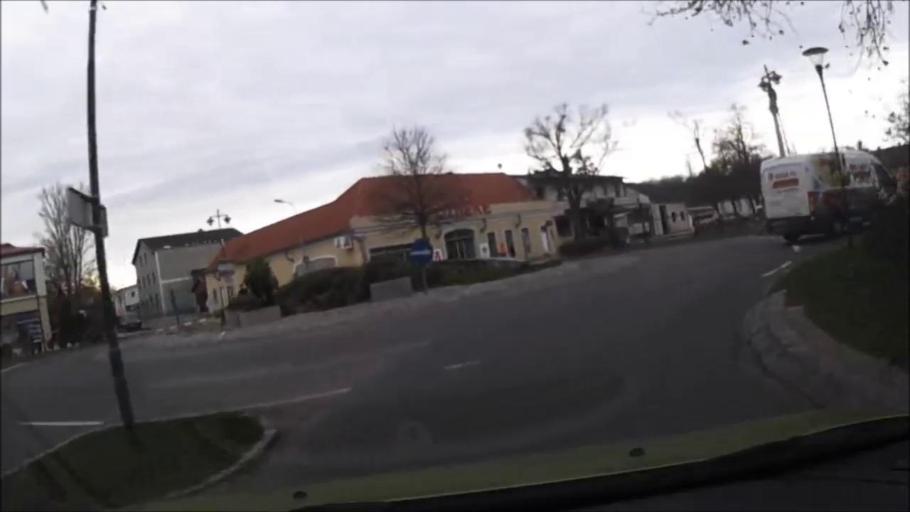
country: AT
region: Lower Austria
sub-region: Politischer Bezirk Baden
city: Ebreichsdorf
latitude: 47.9609
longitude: 16.4312
